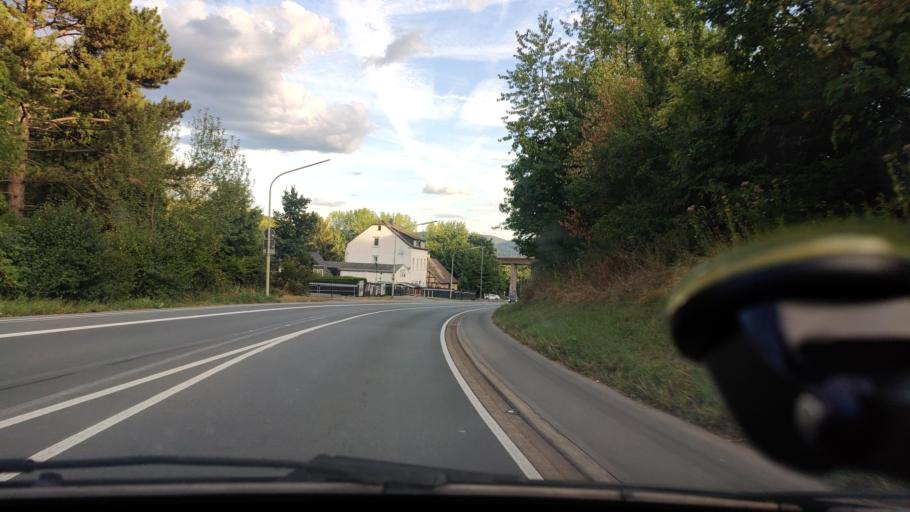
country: DE
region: North Rhine-Westphalia
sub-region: Regierungsbezirk Arnsberg
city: Nachrodt-Wiblingwerde
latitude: 51.3746
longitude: 7.6085
